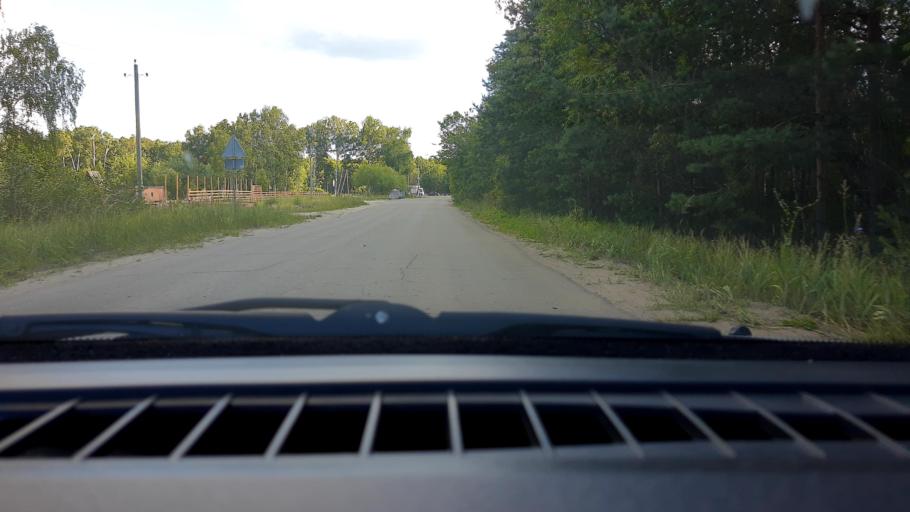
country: RU
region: Nizjnij Novgorod
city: Babino
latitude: 56.3069
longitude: 43.6325
